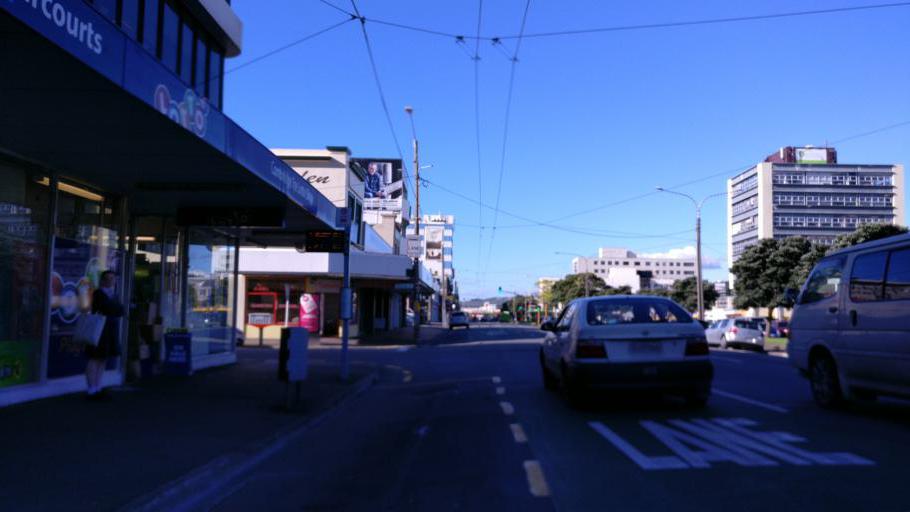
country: NZ
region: Wellington
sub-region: Wellington City
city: Wellington
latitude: -41.2968
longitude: 174.7820
